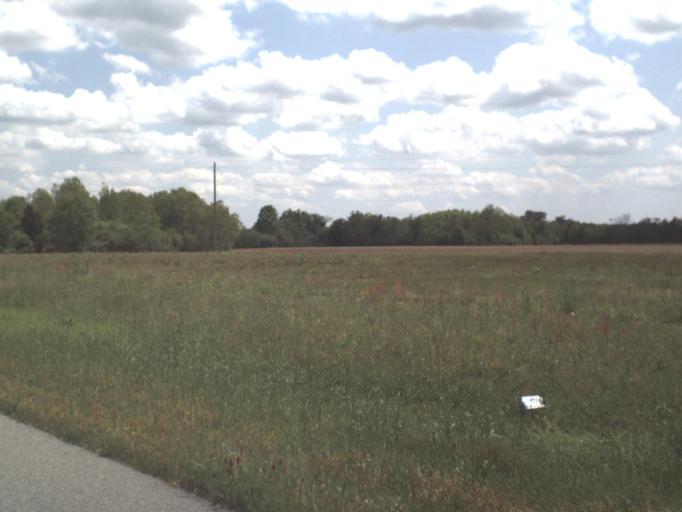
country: US
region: Florida
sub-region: Escambia County
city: Molino
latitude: 30.7399
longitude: -87.3594
